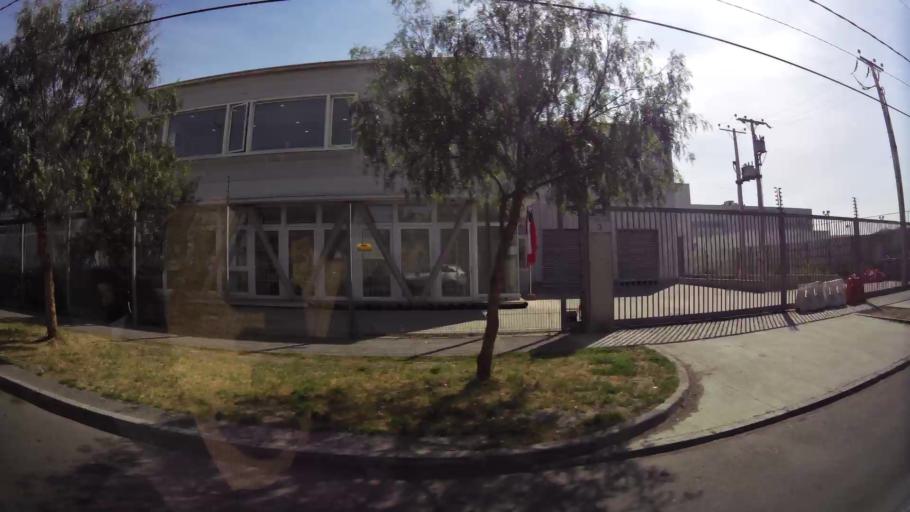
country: CL
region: Santiago Metropolitan
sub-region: Provincia de Santiago
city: Lo Prado
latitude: -33.4313
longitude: -70.7740
